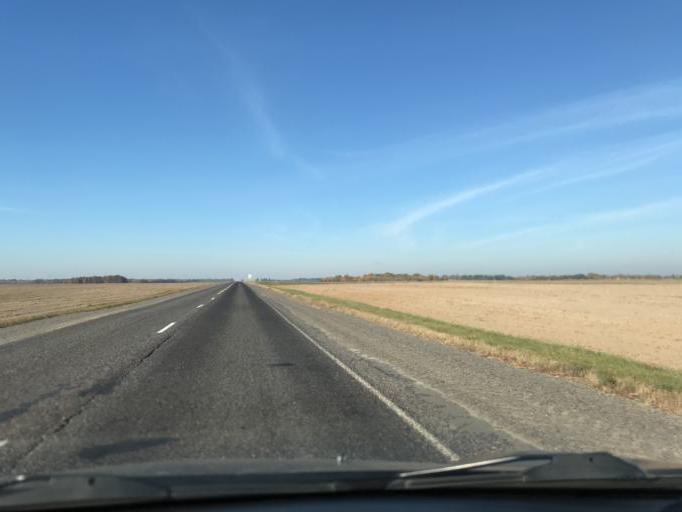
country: BY
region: Gomel
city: Brahin
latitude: 51.7875
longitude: 30.1937
